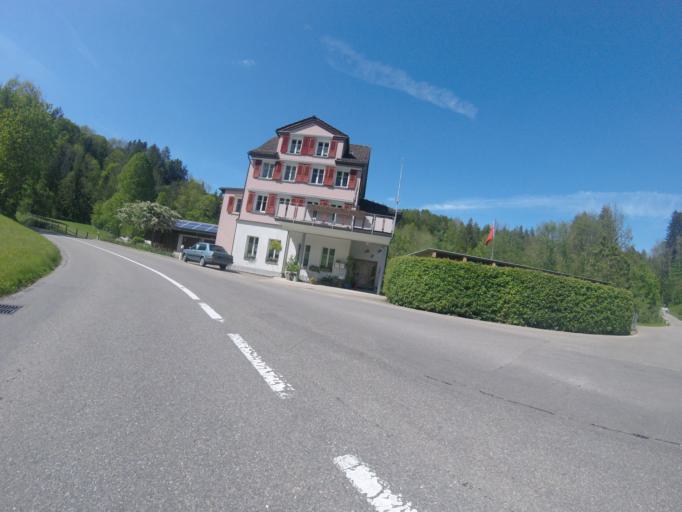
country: CH
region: Saint Gallen
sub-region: Wahlkreis Toggenburg
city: Mogelsberg
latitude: 47.3691
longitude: 9.1391
